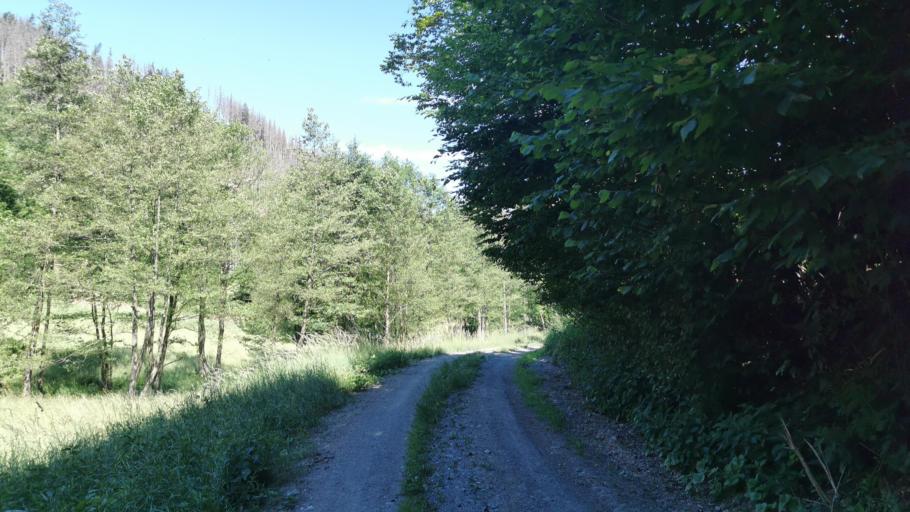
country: DE
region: Thuringia
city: Probstzella
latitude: 50.5507
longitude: 11.3844
